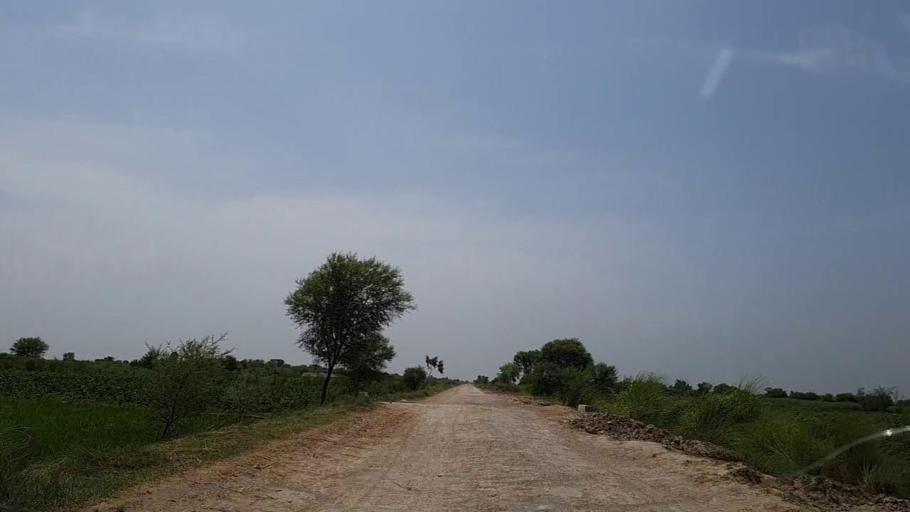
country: PK
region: Sindh
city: Khanpur
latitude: 27.8794
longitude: 69.4919
